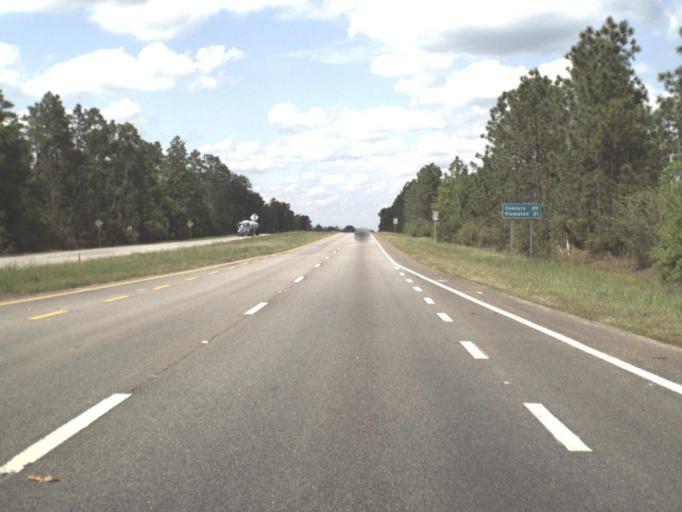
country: US
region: Florida
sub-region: Escambia County
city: Molino
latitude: 30.7319
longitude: -87.3491
